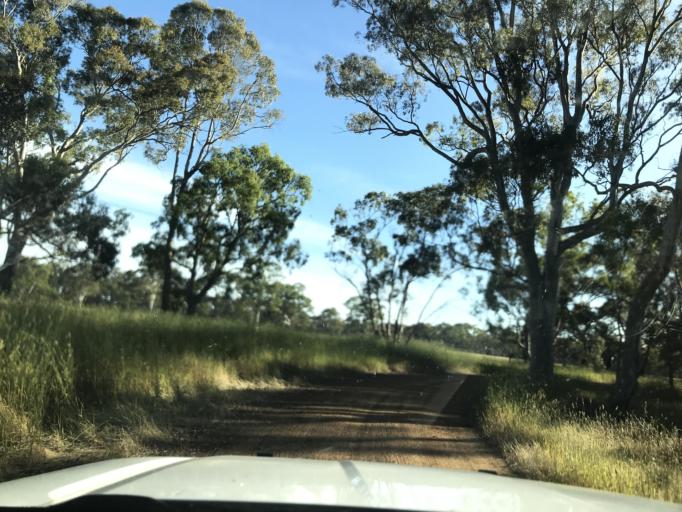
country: AU
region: South Australia
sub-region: Wattle Range
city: Penola
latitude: -37.1193
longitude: 141.4422
